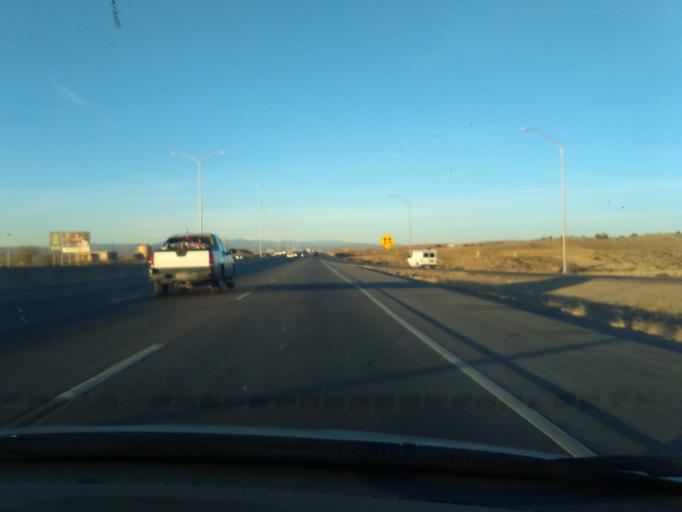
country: US
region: New Mexico
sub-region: Sandoval County
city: Corrales
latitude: 35.2062
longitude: -106.5764
